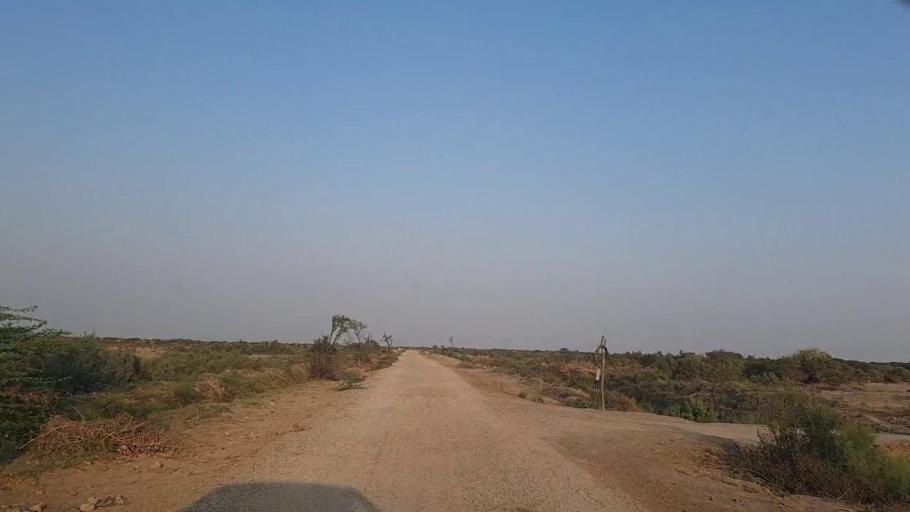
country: PK
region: Sindh
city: Jati
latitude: 24.4889
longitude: 68.4116
